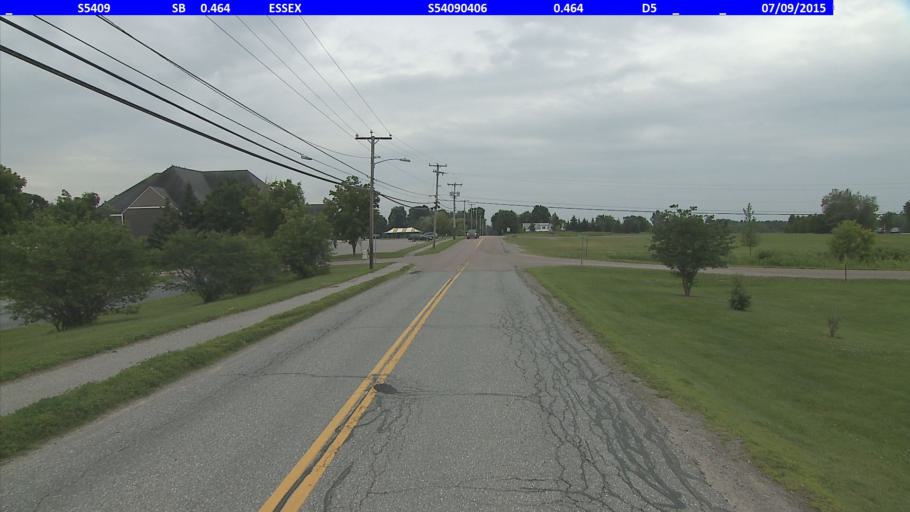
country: US
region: Vermont
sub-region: Chittenden County
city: Essex Junction
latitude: 44.5166
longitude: -73.0816
